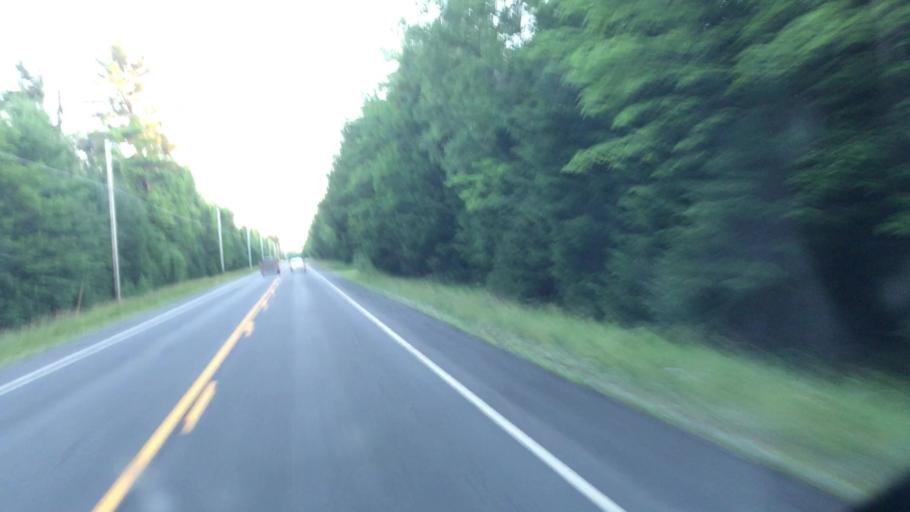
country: US
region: Maine
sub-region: Penobscot County
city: Medway
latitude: 45.5850
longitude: -68.3157
